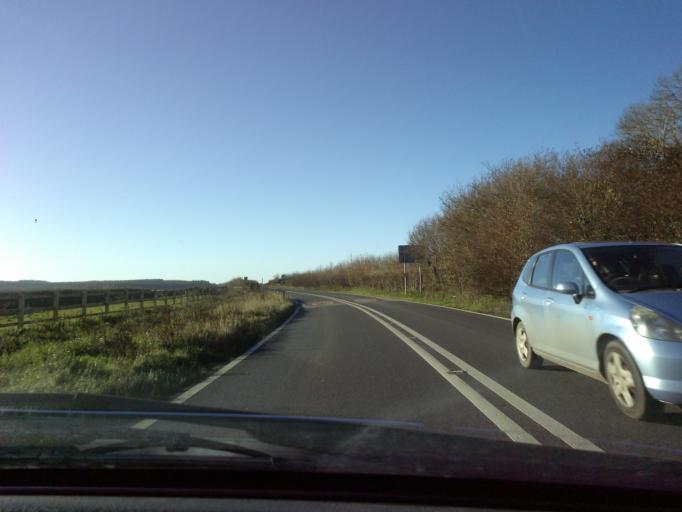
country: GB
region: England
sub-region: Dorset
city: Blandford Forum
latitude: 50.7729
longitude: -2.1673
